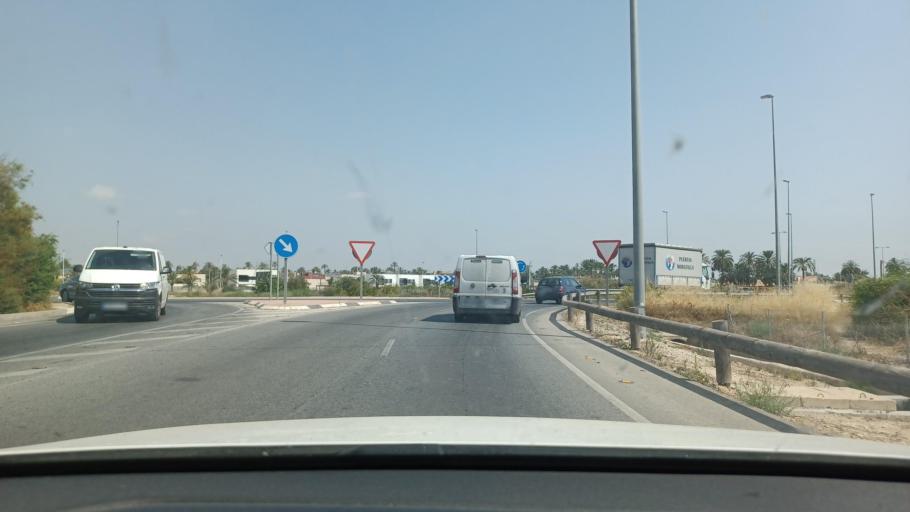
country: ES
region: Valencia
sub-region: Provincia de Alicante
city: Elche
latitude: 38.2517
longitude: -0.6920
